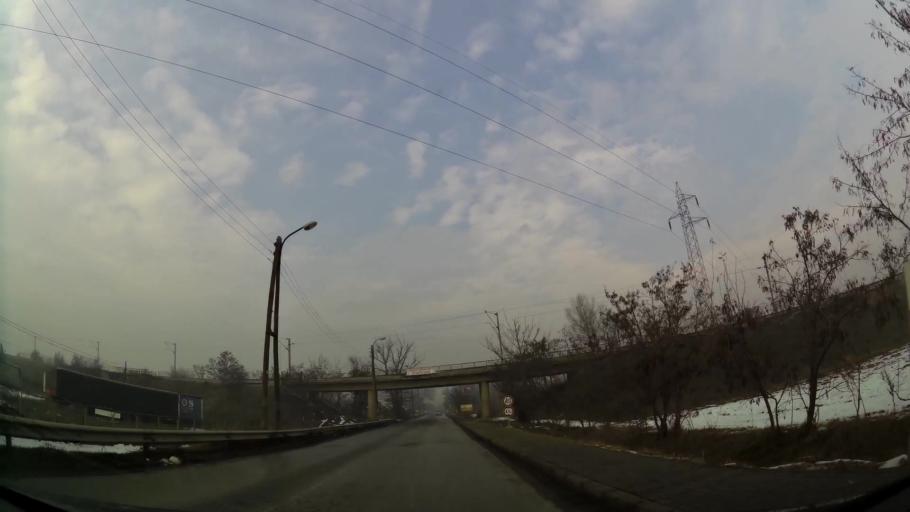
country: MK
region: Kisela Voda
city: Kisela Voda
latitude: 41.9902
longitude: 21.5116
